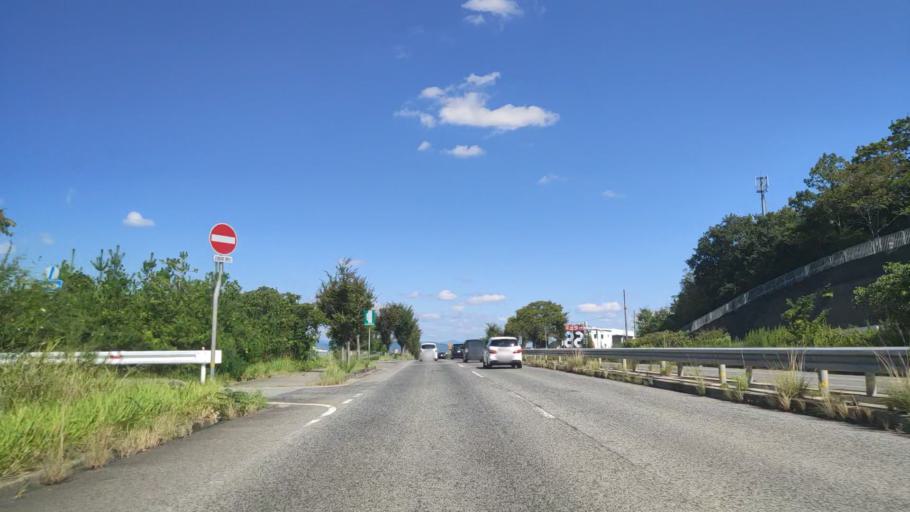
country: JP
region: Hyogo
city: Ono
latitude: 34.8506
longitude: 134.9498
